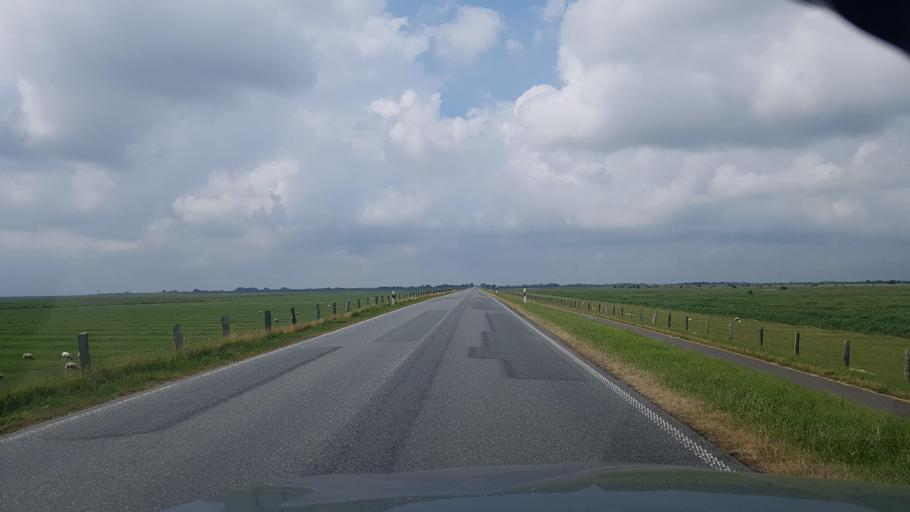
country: DE
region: Schleswig-Holstein
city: Wobbenbull
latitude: 54.5225
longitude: 8.9745
